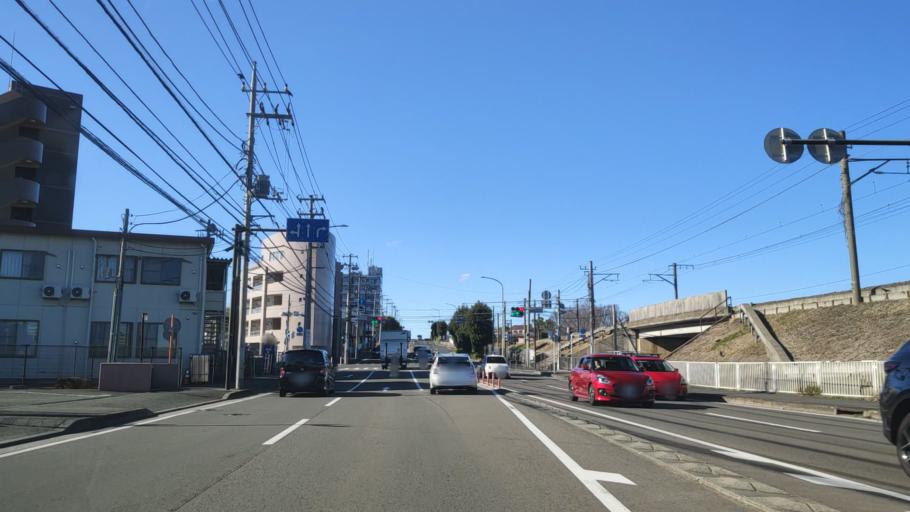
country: JP
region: Tokyo
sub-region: Machida-shi
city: Machida
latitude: 35.5195
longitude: 139.5297
